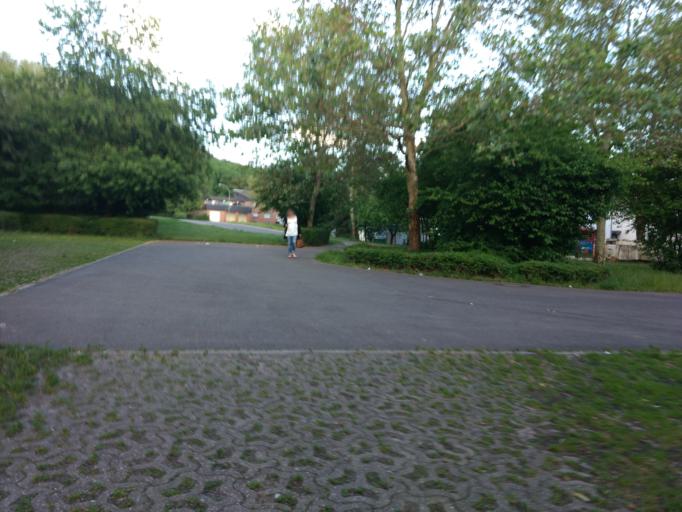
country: DE
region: Saarland
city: Saarlouis
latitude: 49.3350
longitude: 6.7597
